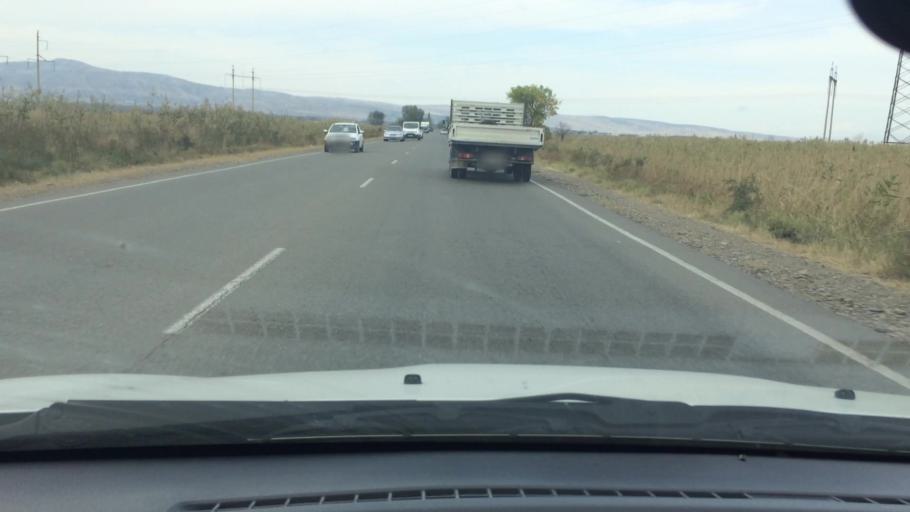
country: GE
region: Kvemo Kartli
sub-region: Marneuli
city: Marneuli
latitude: 41.5412
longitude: 44.7768
